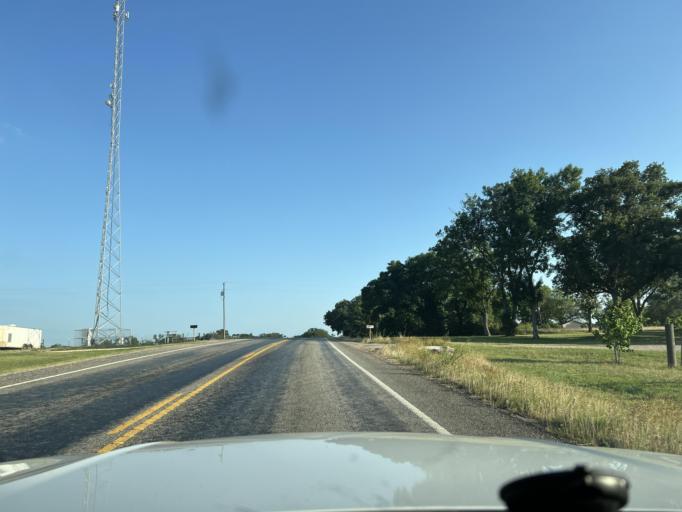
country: US
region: Texas
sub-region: Washington County
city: Brenham
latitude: 30.2099
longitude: -96.3637
